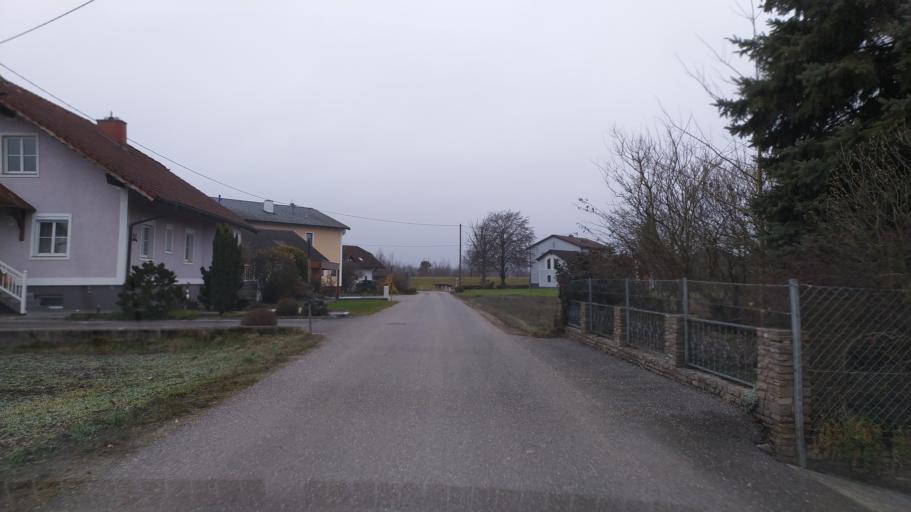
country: AT
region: Lower Austria
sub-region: Politischer Bezirk Amstetten
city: Strengberg
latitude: 48.1908
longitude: 14.7199
